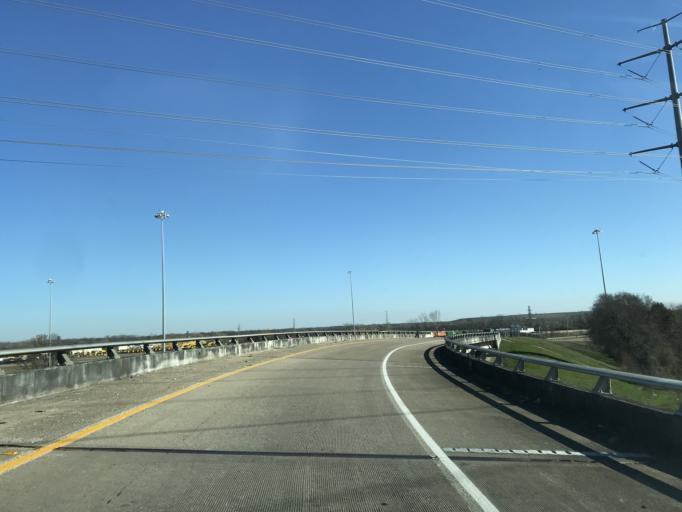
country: US
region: Texas
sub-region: Dallas County
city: Hutchins
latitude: 32.6998
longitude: -96.7553
